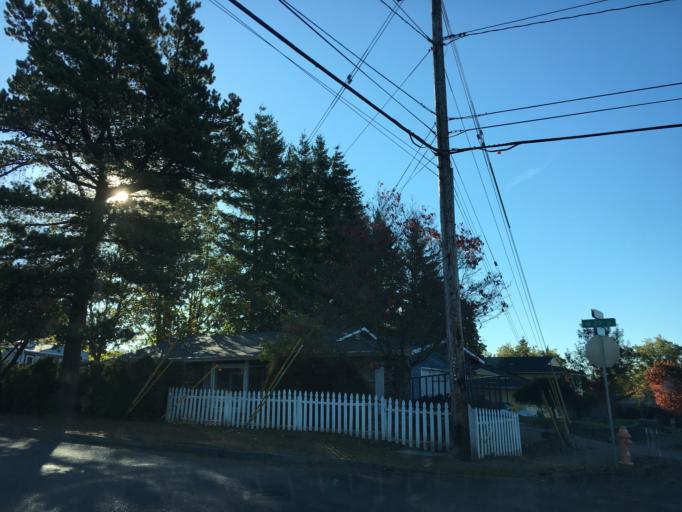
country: US
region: Oregon
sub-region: Multnomah County
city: Wood Village
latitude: 45.5132
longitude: -122.4125
